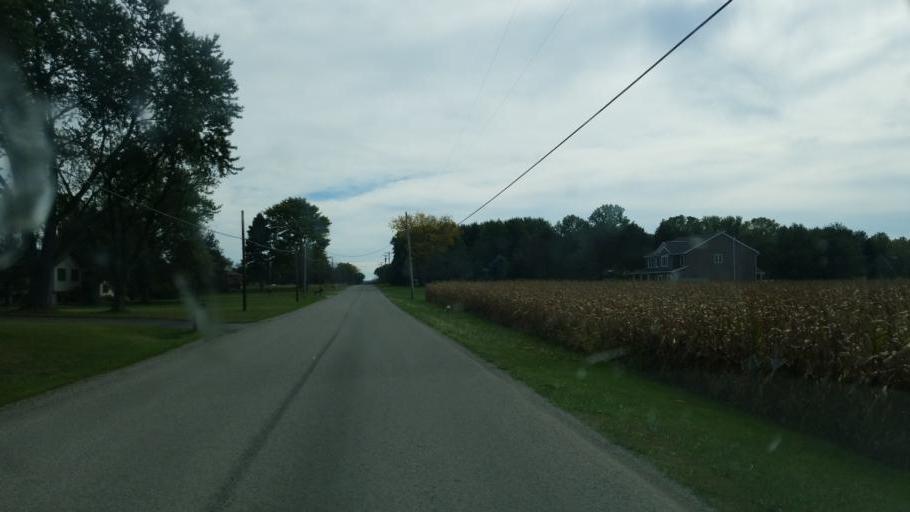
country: US
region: Ohio
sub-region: Erie County
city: Huron
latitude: 41.3784
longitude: -82.5317
